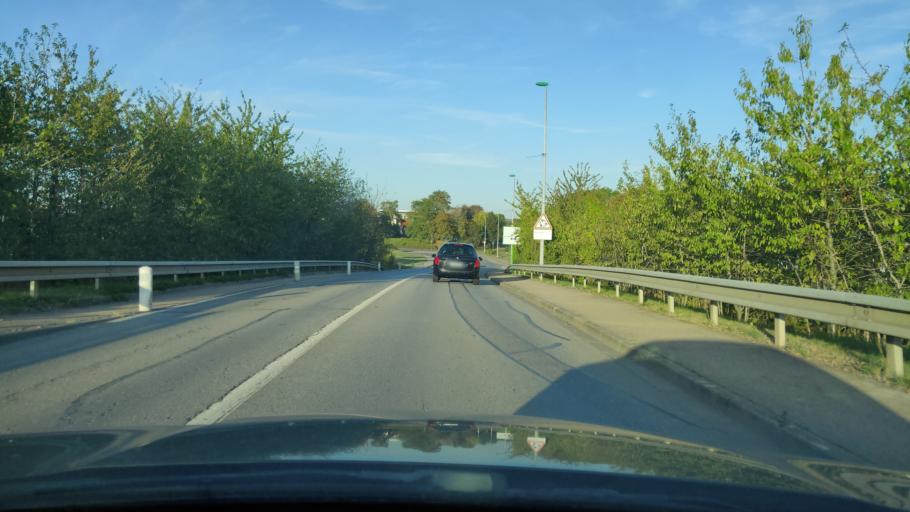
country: FR
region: Lorraine
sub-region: Departement de la Moselle
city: Maizieres-les-Metz
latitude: 49.2116
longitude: 6.1514
